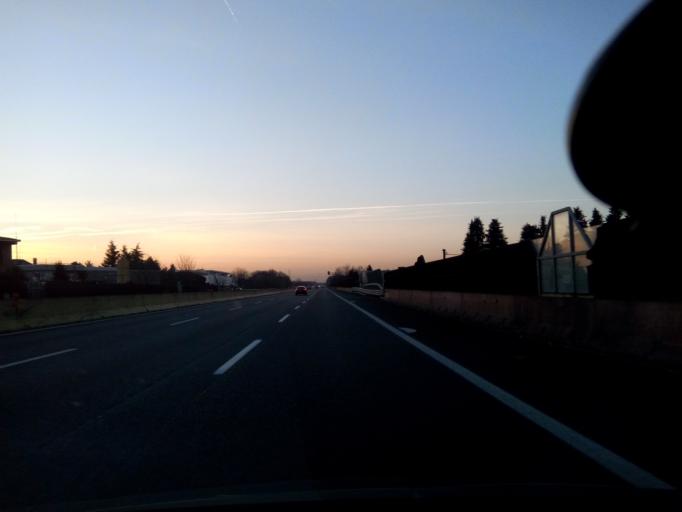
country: IT
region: Lombardy
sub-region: Citta metropolitana di Milano
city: Cerro Maggiore
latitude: 45.5980
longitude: 8.9570
